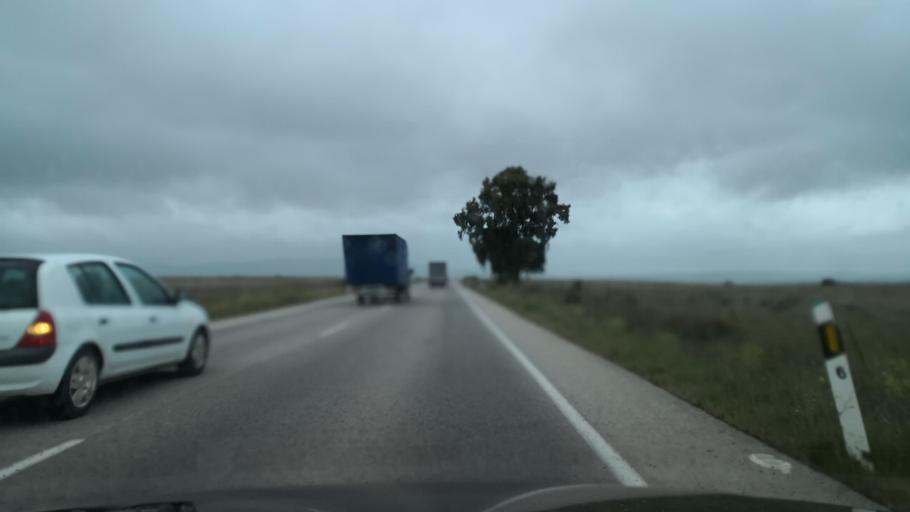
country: ES
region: Extremadura
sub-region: Provincia de Caceres
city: Malpartida de Caceres
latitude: 39.3527
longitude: -6.4683
